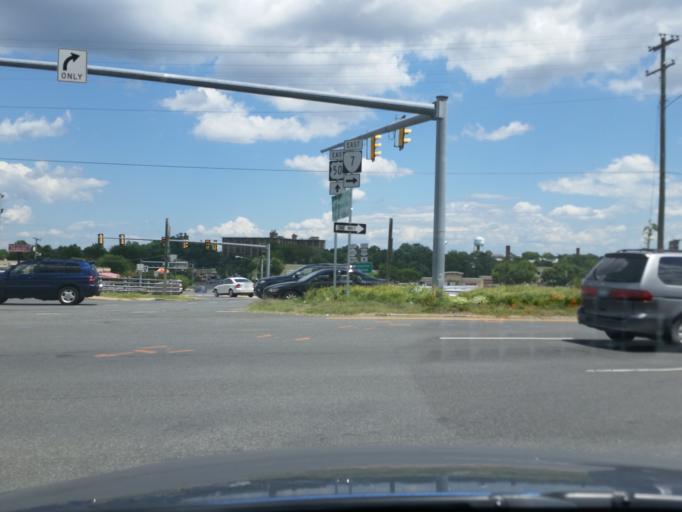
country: US
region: Virginia
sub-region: Fairfax County
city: Seven Corners
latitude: 38.8718
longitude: -77.1559
